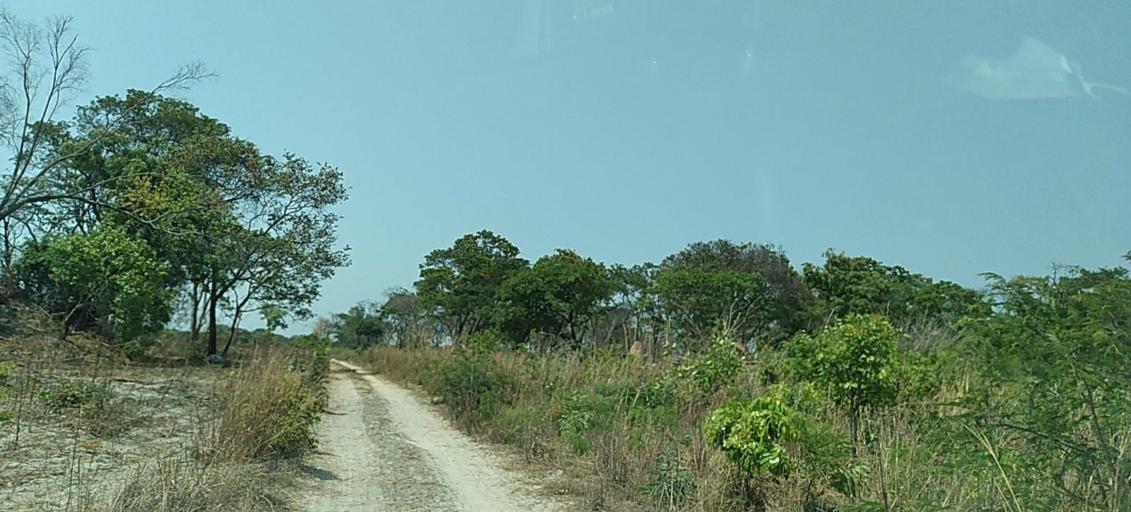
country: ZM
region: Copperbelt
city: Mpongwe
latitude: -13.8401
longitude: 28.0594
